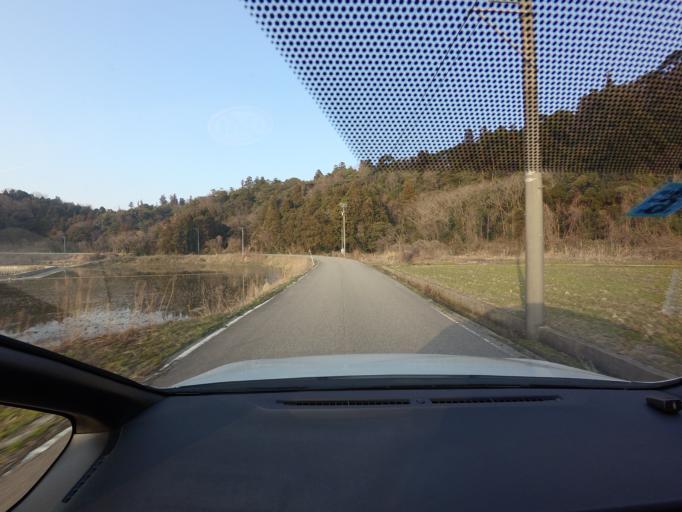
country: JP
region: Ishikawa
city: Nanao
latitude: 37.1470
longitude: 137.0245
